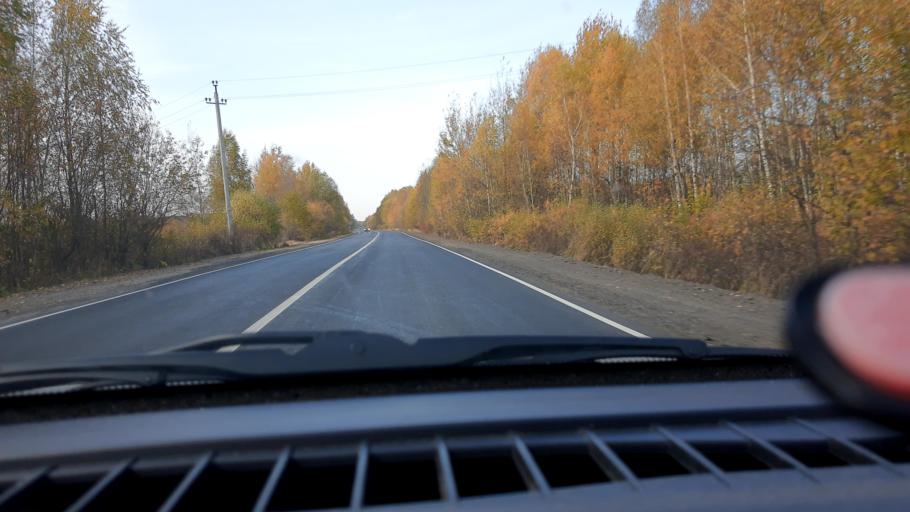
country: RU
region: Nizjnij Novgorod
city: Lukino
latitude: 56.5323
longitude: 43.8016
